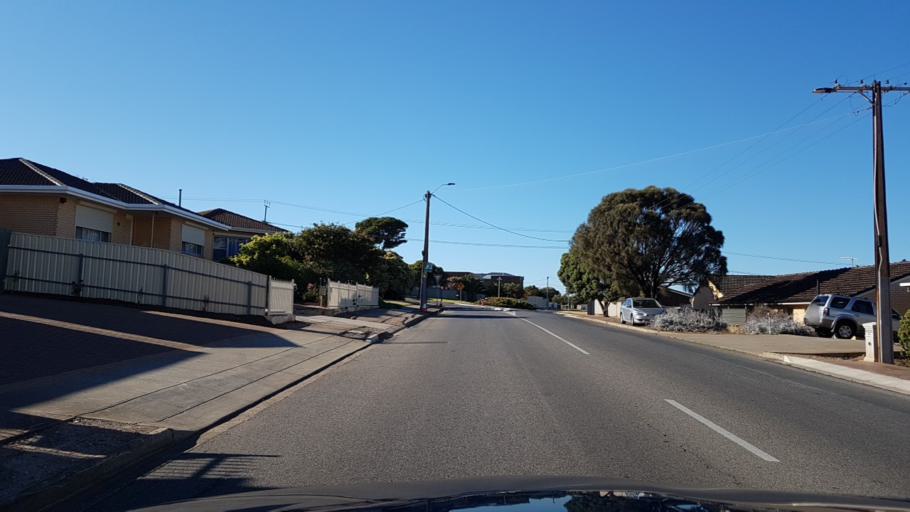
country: AU
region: South Australia
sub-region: Adelaide
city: Port Noarlunga
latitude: -35.1345
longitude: 138.4733
